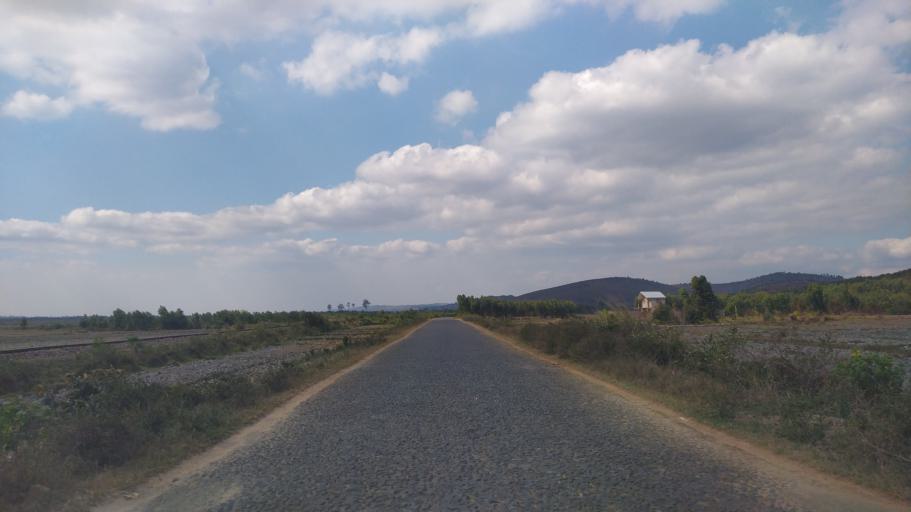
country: MG
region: Alaotra Mangoro
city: Moramanga
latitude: -18.7650
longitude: 48.2544
